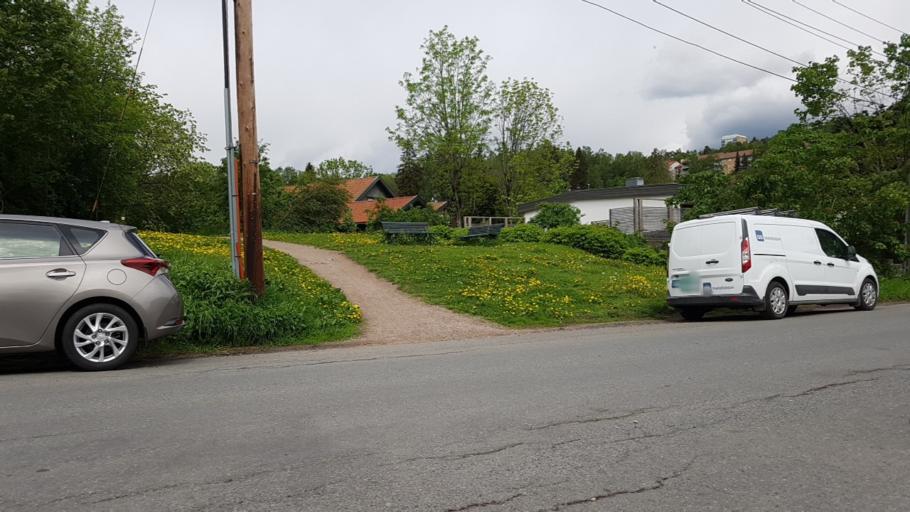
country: NO
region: Oslo
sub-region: Oslo
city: Oslo
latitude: 59.9416
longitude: 10.8220
